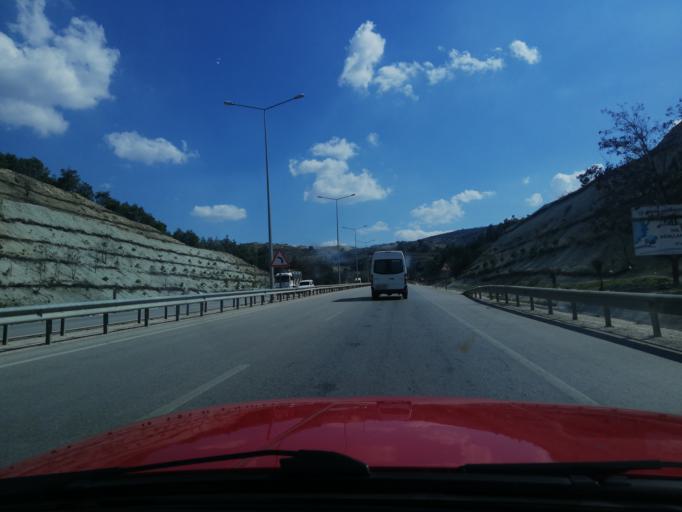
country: TR
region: Burdur
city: Burdur
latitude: 37.7052
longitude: 30.3062
